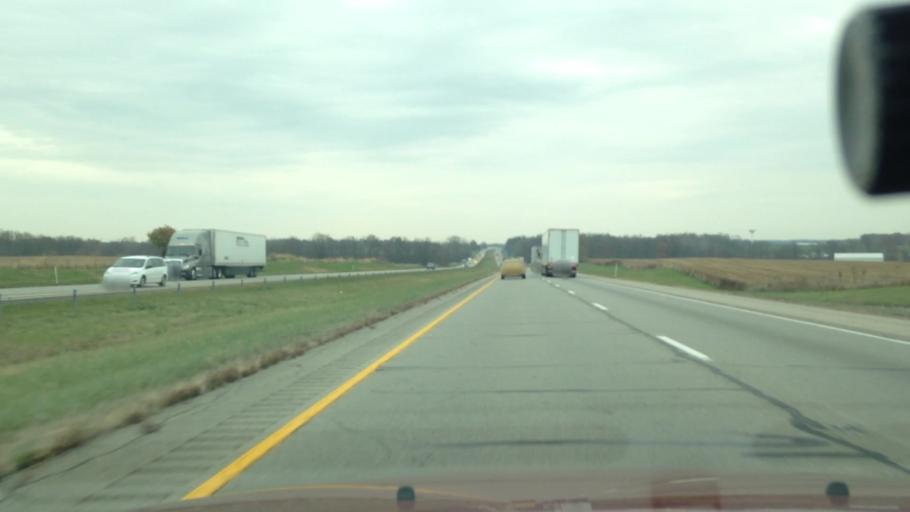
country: US
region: Indiana
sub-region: Wayne County
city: Cambridge City
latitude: 39.8531
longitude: -85.1815
